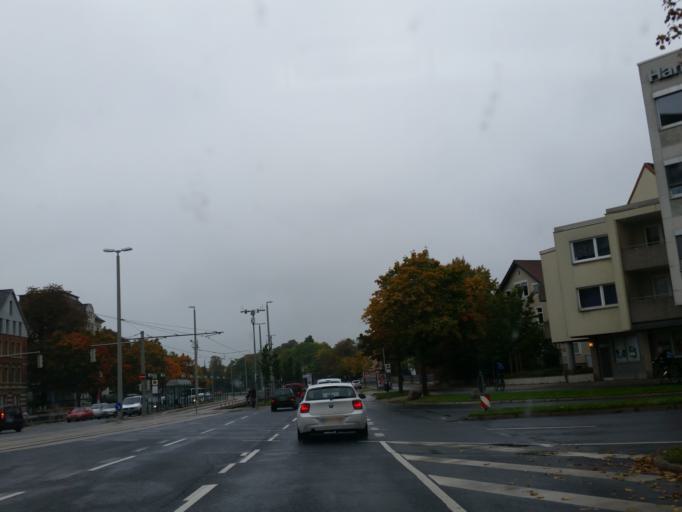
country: DE
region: Lower Saxony
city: Braunschweig
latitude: 52.2566
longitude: 10.5339
